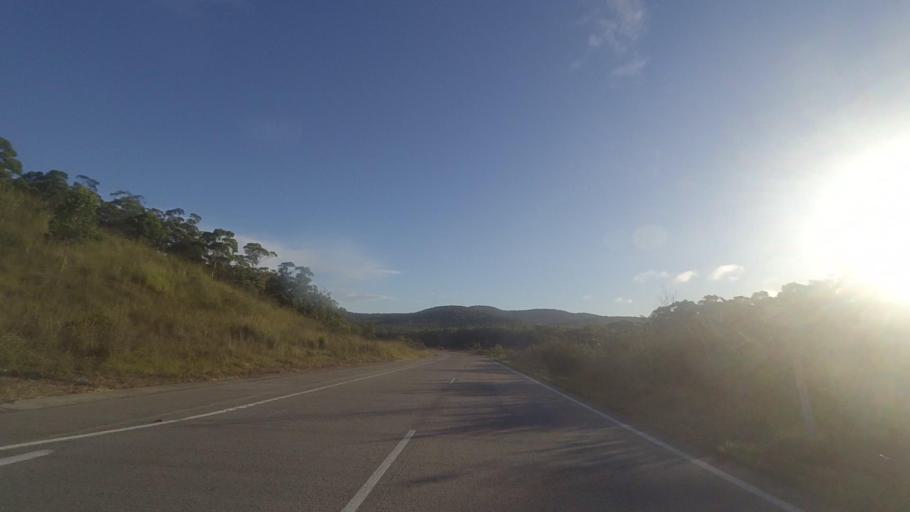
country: AU
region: New South Wales
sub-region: Great Lakes
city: Bulahdelah
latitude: -32.4782
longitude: 152.1937
